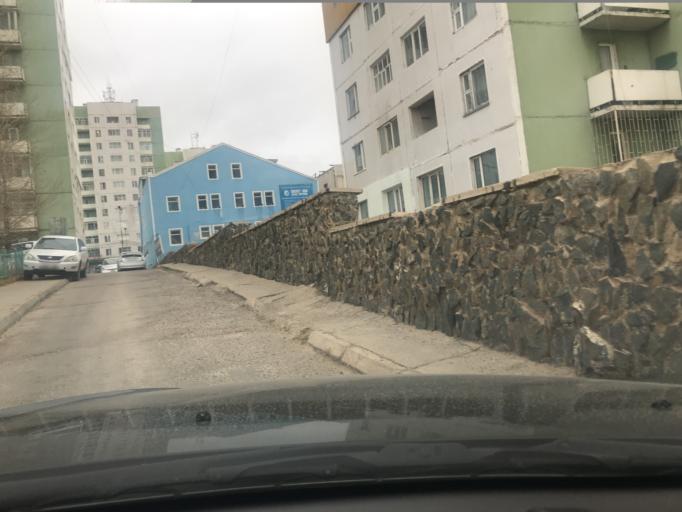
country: MN
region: Ulaanbaatar
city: Ulaanbaatar
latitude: 47.9232
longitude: 106.9412
